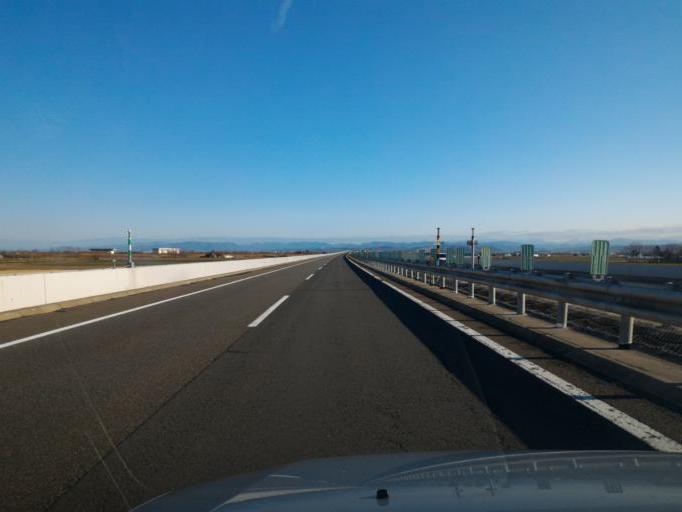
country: JP
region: Hokkaido
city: Iwamizawa
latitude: 43.1449
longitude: 141.6827
